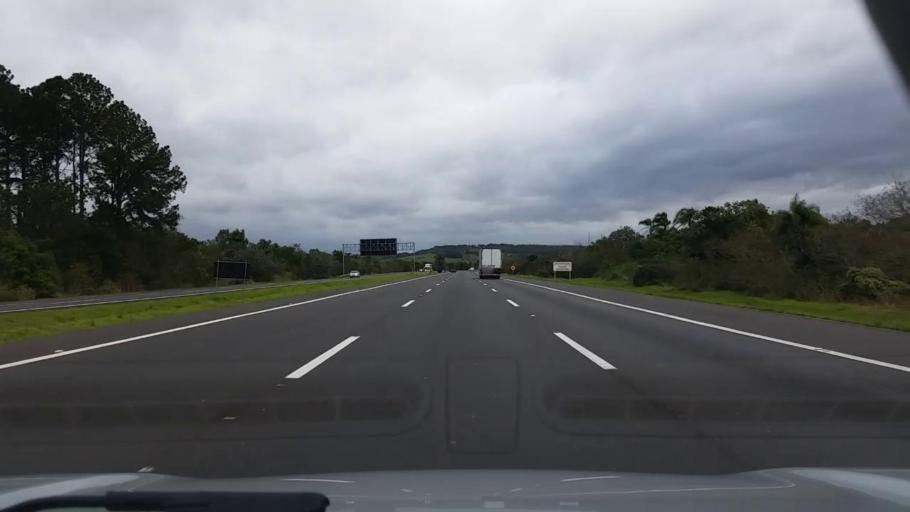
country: BR
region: Rio Grande do Sul
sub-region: Osorio
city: Osorio
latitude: -29.8877
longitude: -50.4555
